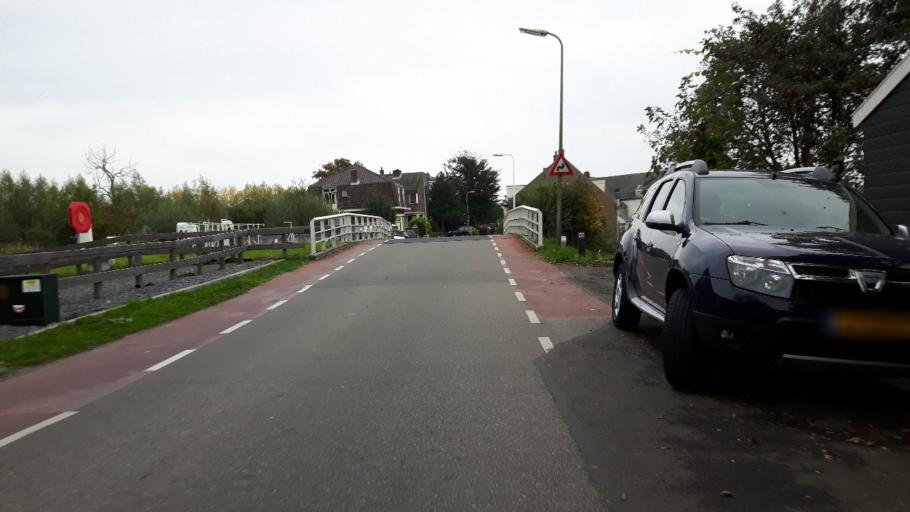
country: NL
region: South Holland
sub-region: Gemeente Gouda
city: Gouda
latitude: 52.0053
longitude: 4.7176
